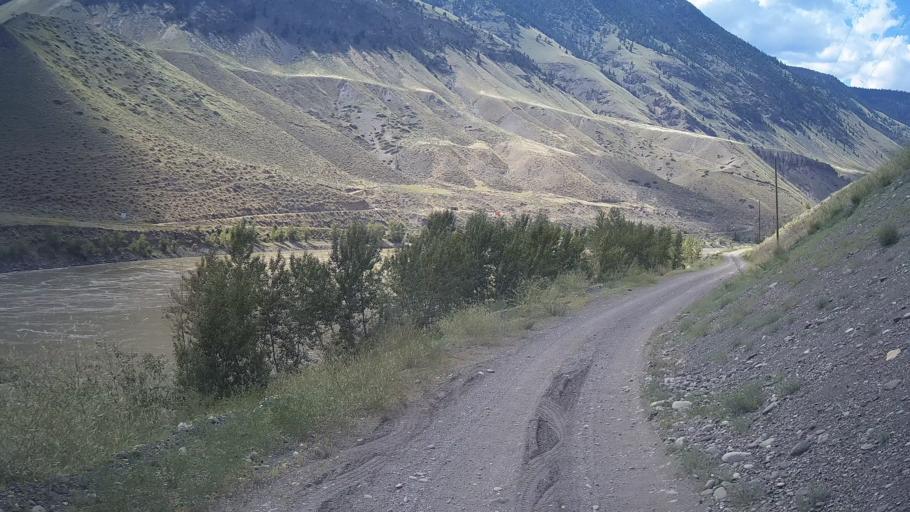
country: CA
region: British Columbia
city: Lillooet
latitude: 51.1823
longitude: -122.1266
